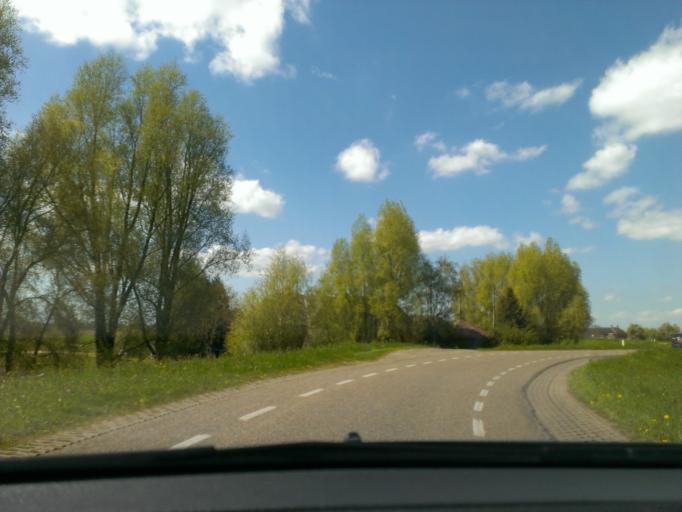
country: NL
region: Overijssel
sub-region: Gemeente Olst-Wijhe
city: Olst
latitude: 52.3517
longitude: 6.0863
